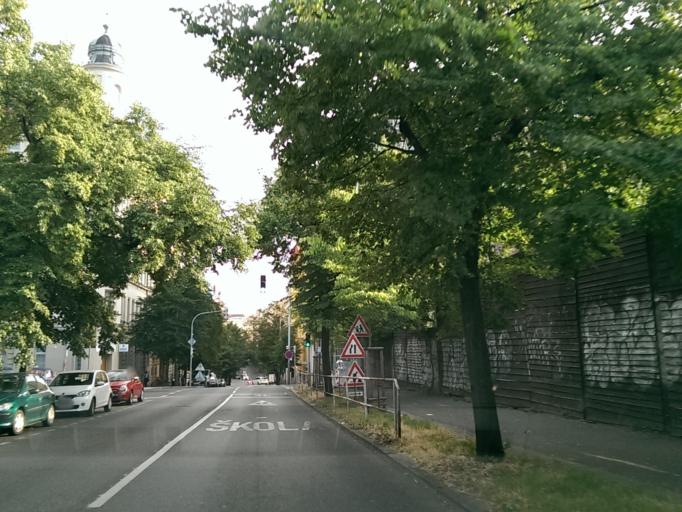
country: CZ
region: Praha
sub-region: Praha 8
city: Karlin
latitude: 50.0797
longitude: 14.4376
